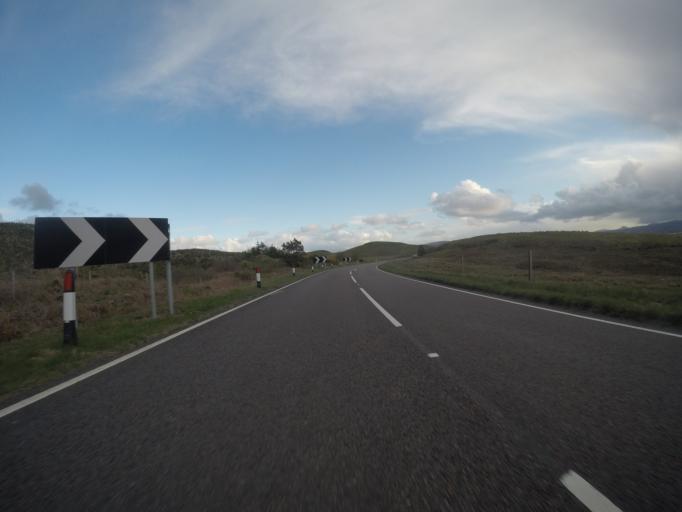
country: GB
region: Scotland
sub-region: Highland
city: Portree
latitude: 57.5492
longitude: -6.3636
